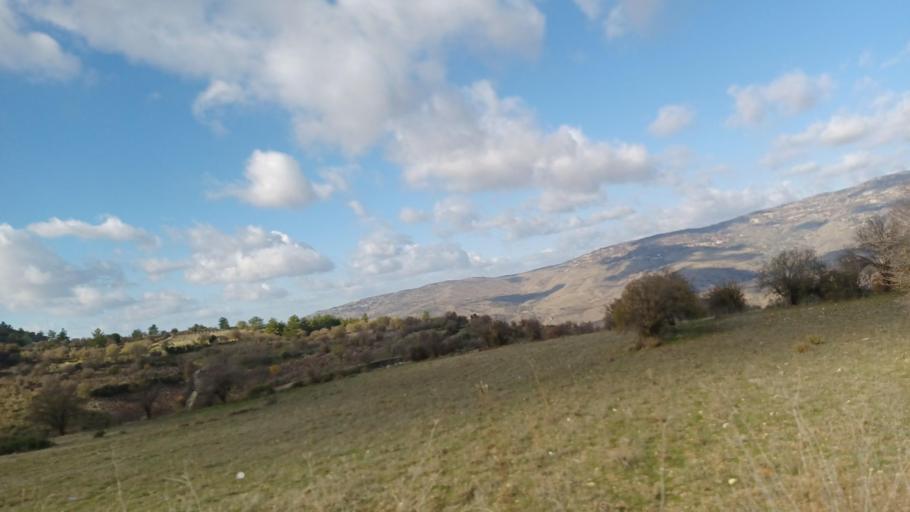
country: CY
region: Limassol
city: Pachna
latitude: 34.8564
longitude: 32.6911
